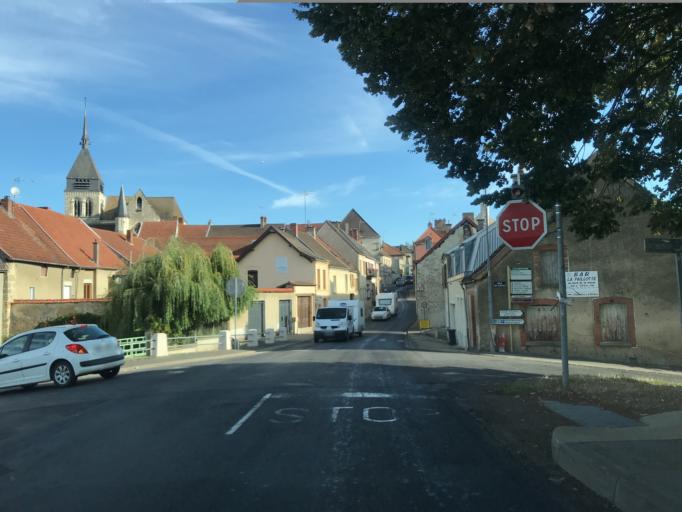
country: FR
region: Champagne-Ardenne
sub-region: Departement de la Marne
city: Damery
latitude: 49.0699
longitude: 3.8774
